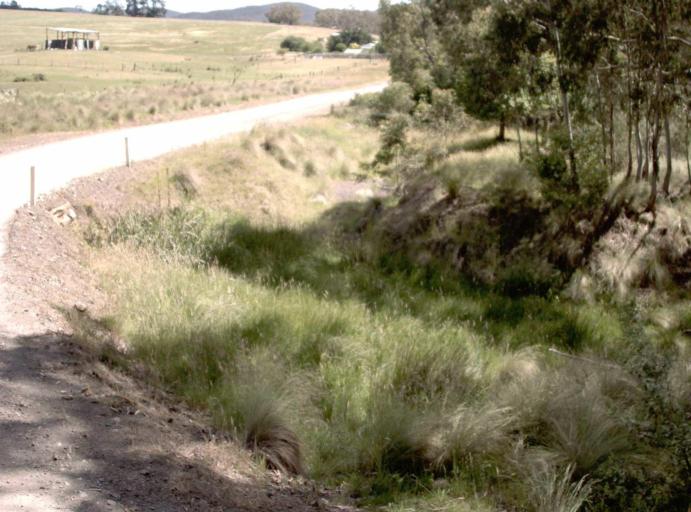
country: AU
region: New South Wales
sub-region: Bombala
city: Bombala
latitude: -37.1312
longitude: 148.6665
